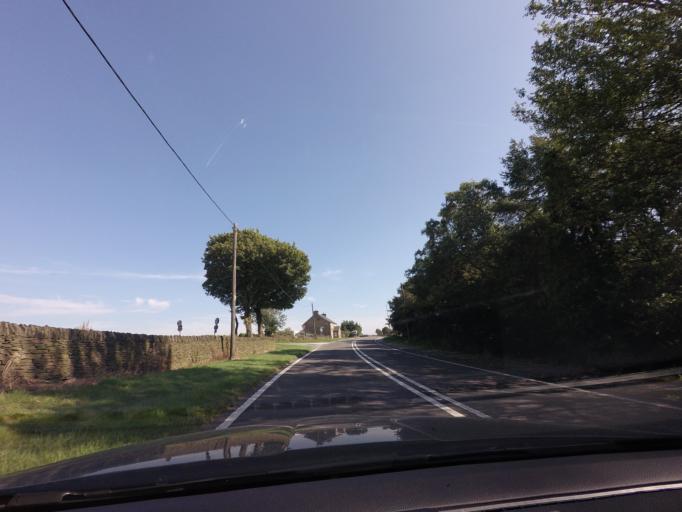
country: GB
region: England
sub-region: Derbyshire
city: Dronfield
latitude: 53.2376
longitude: -1.5367
